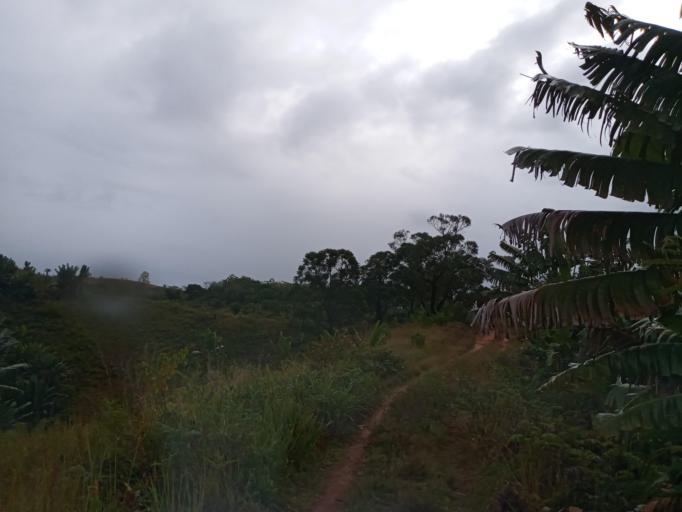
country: MG
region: Atsimo-Atsinanana
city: Vohipaho
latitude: -23.9966
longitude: 47.4022
